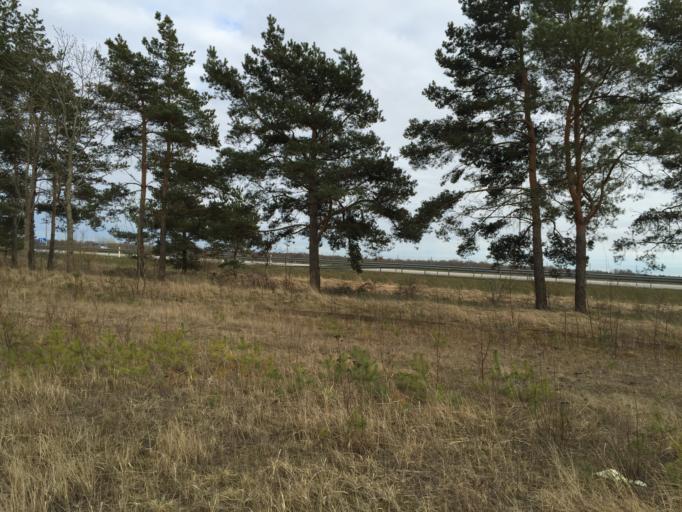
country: LT
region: Klaipedos apskritis
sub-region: Klaipeda
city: Klaipeda
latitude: 55.7096
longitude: 21.2475
